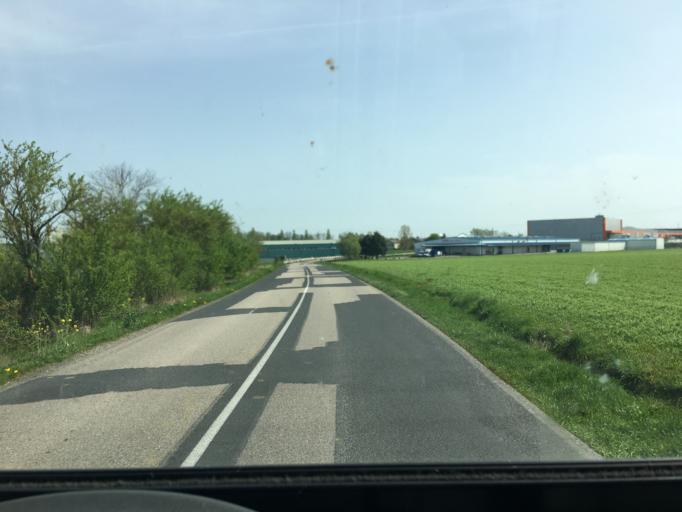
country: FR
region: Lorraine
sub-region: Departement de Meurthe-et-Moselle
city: Art-sur-Meurthe
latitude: 48.6154
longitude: 6.2621
